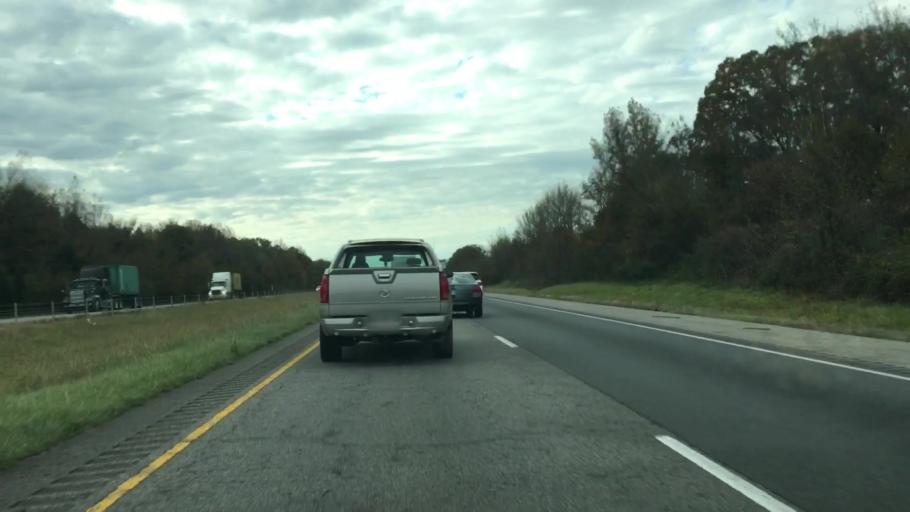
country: US
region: Arkansas
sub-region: Conway County
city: Morrilton
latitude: 35.1624
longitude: -92.6123
